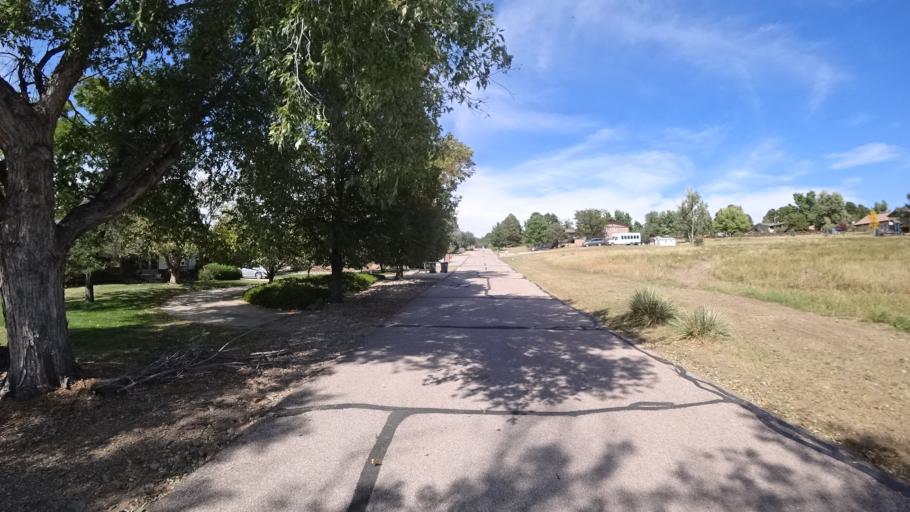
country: US
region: Colorado
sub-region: El Paso County
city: Cimarron Hills
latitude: 38.9075
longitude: -104.7593
